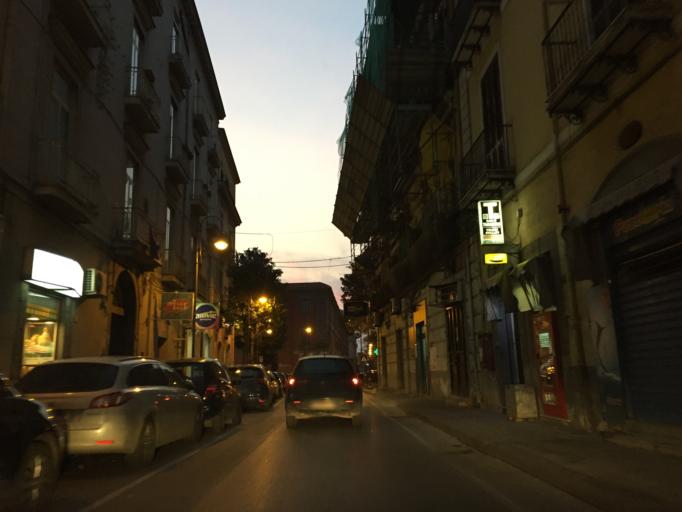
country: IT
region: Campania
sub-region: Provincia di Salerno
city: Nocera Inferiore
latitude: 40.7465
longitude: 14.6446
